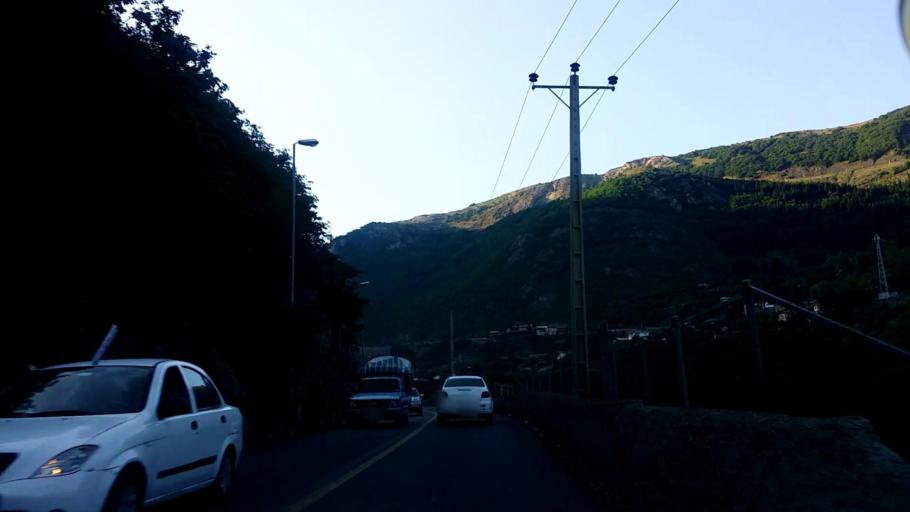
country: IR
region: Tehran
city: Tajrish
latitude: 36.2188
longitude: 51.3125
